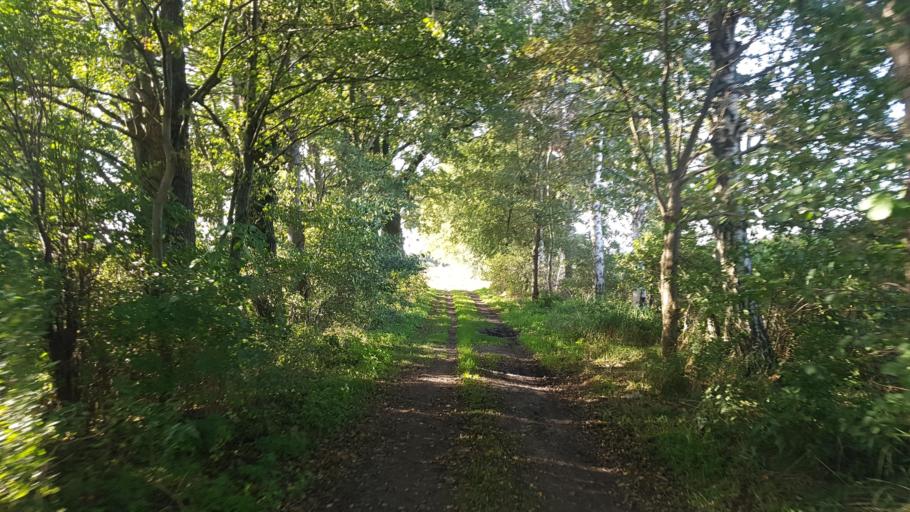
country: DE
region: Brandenburg
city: Schraden
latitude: 51.4238
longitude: 13.7154
